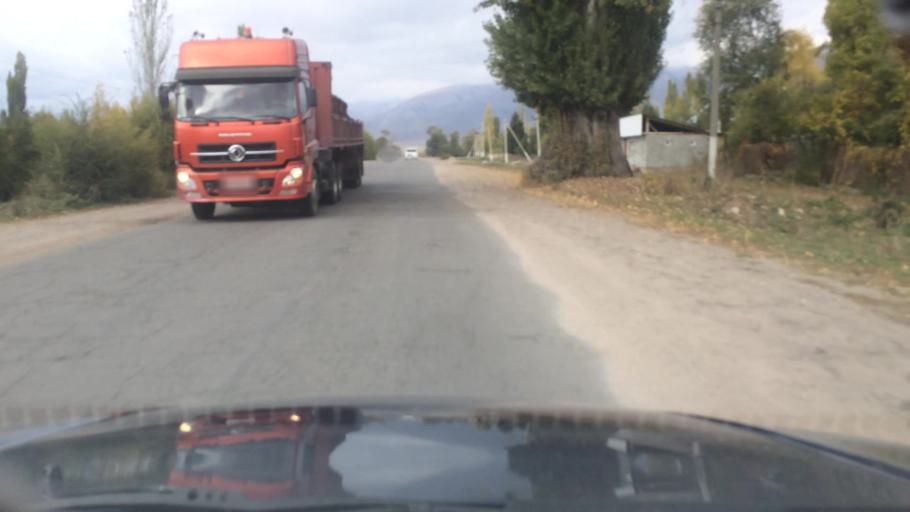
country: KG
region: Ysyk-Koel
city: Tyup
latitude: 42.7821
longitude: 78.2872
